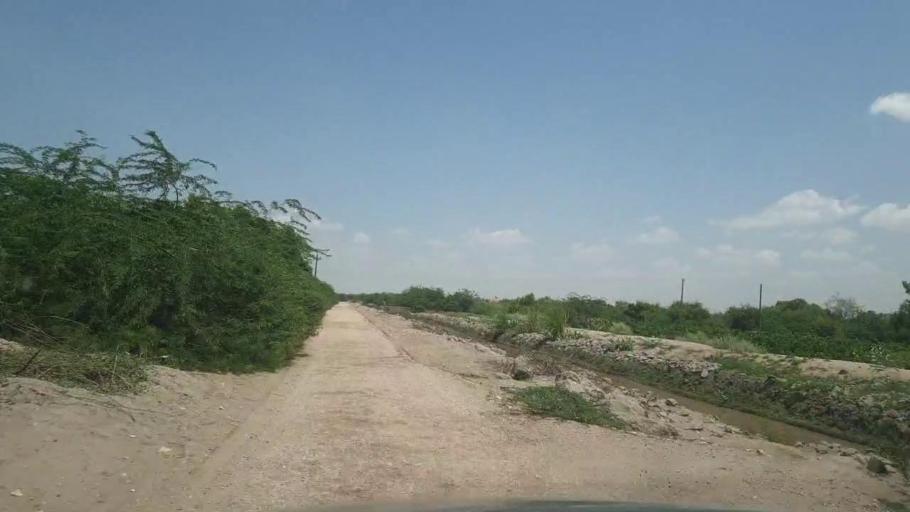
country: PK
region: Sindh
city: Kot Diji
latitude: 27.2935
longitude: 69.0688
